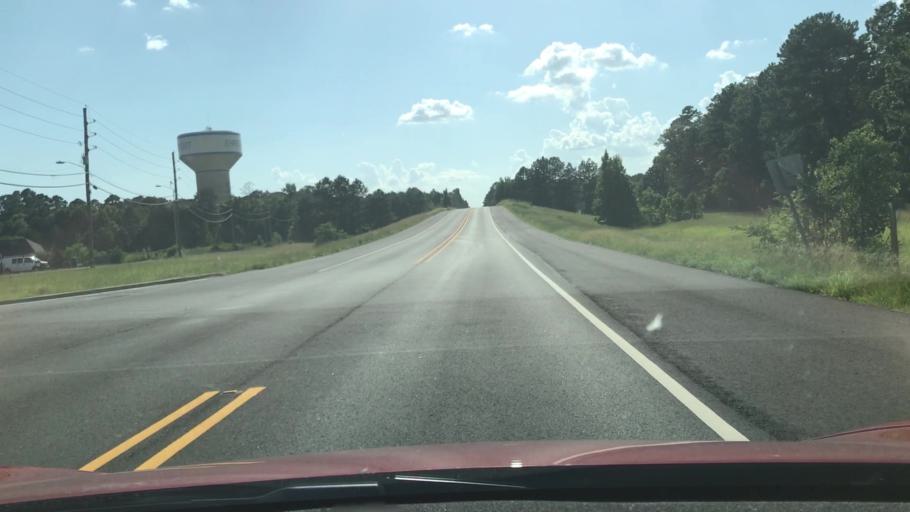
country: US
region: Louisiana
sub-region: Bossier Parish
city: Bossier City
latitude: 32.3910
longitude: -93.7489
